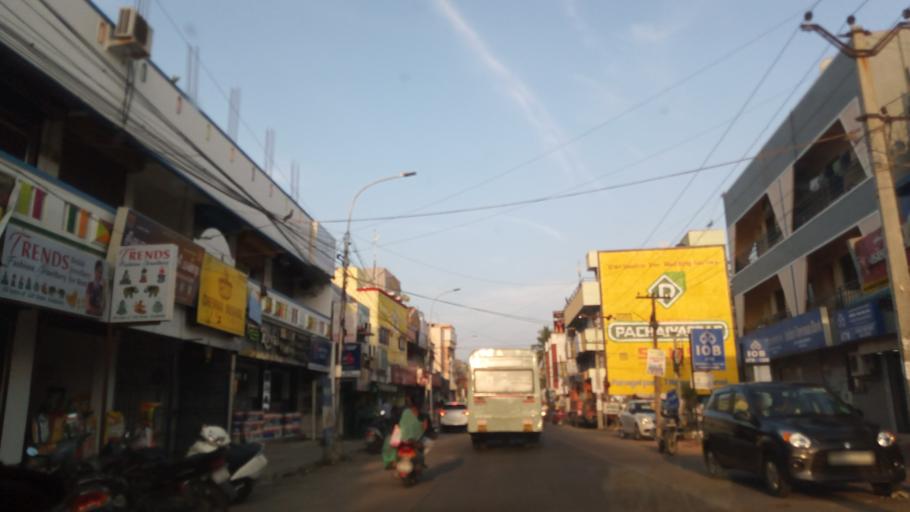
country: IN
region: Tamil Nadu
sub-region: Kancheepuram
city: Manappakkam
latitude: 13.0318
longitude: 80.1851
